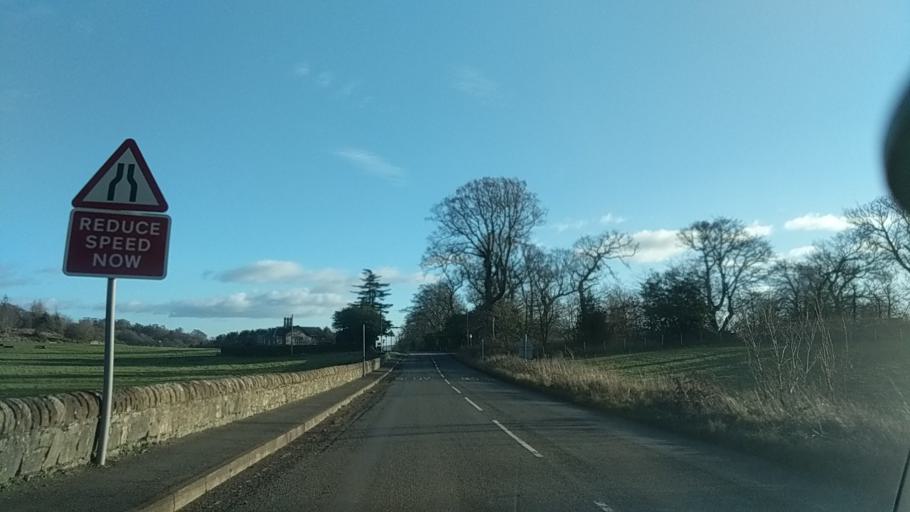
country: GB
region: Scotland
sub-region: Edinburgh
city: Queensferry
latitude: 55.9851
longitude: -3.3610
